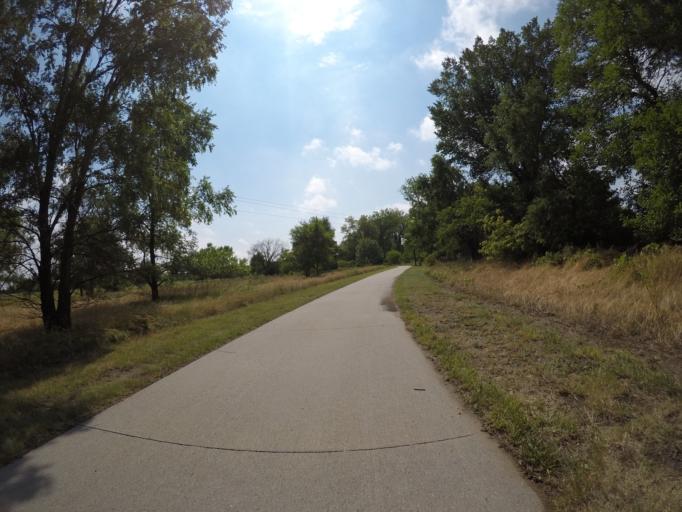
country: US
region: Nebraska
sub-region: Buffalo County
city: Kearney
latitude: 40.6769
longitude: -99.1010
